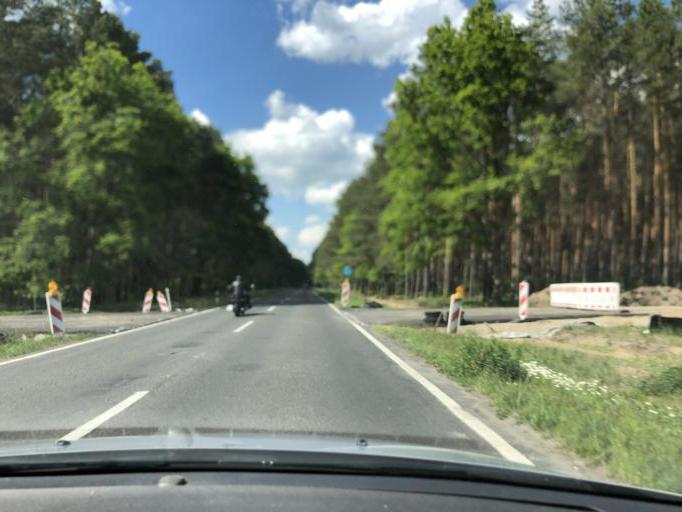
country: DE
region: Brandenburg
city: Spreenhagen
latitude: 52.3703
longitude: 13.8369
